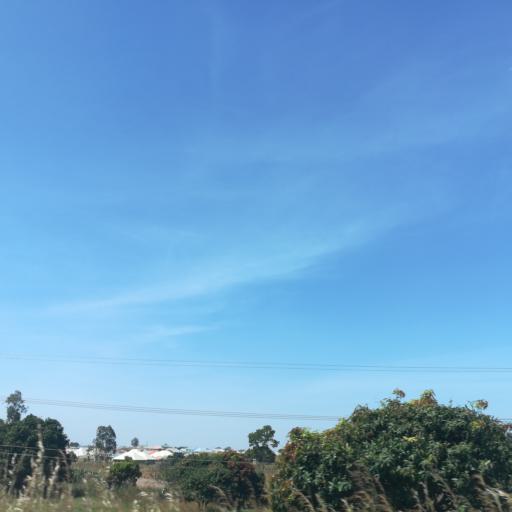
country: NG
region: Plateau
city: Bukuru
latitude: 9.7835
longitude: 8.8831
